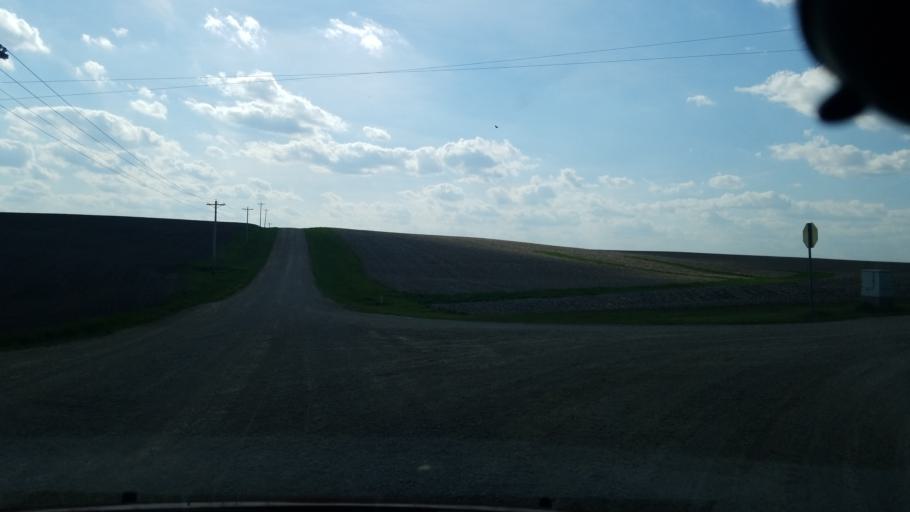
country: US
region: Iowa
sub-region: Jackson County
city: Maquoketa
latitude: 42.2149
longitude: -90.7140
